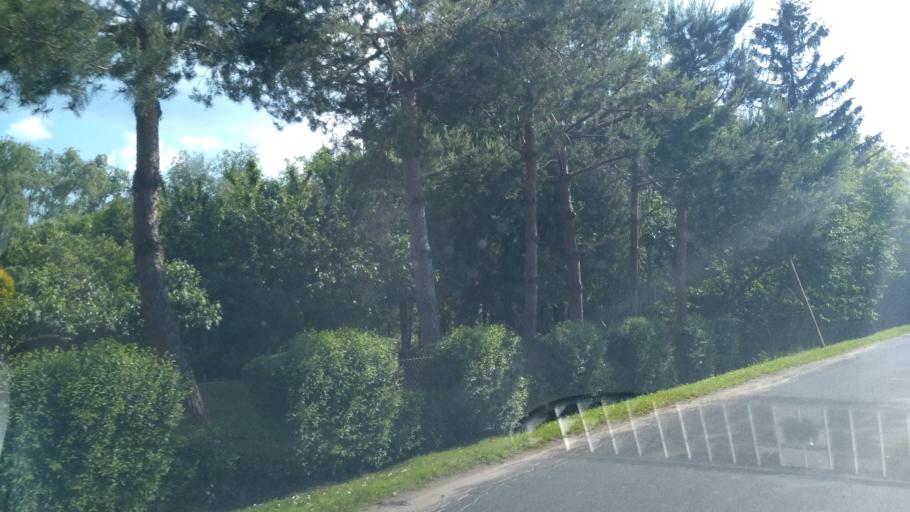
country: PL
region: Subcarpathian Voivodeship
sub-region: Powiat jaroslawski
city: Rokietnica
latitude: 49.9227
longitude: 22.6854
